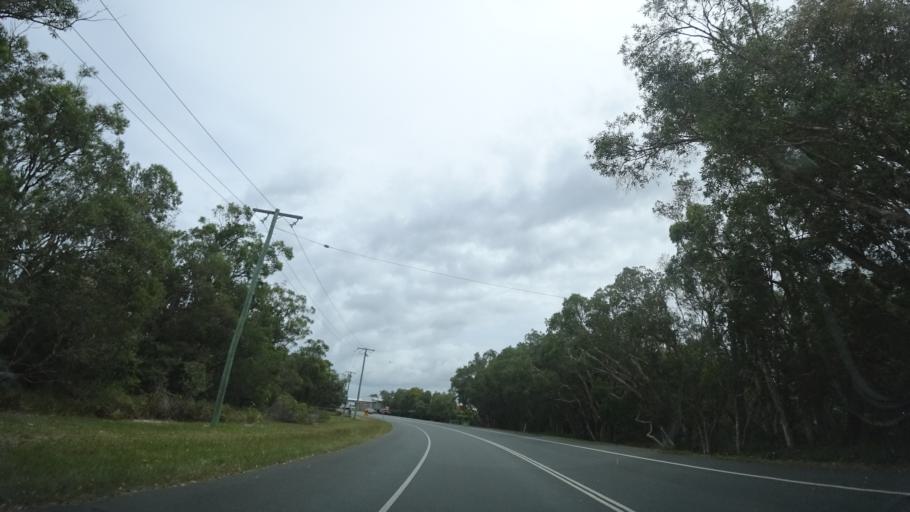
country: AU
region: Queensland
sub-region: Sunshine Coast
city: Coolum Beach
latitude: -26.5640
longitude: 153.0926
